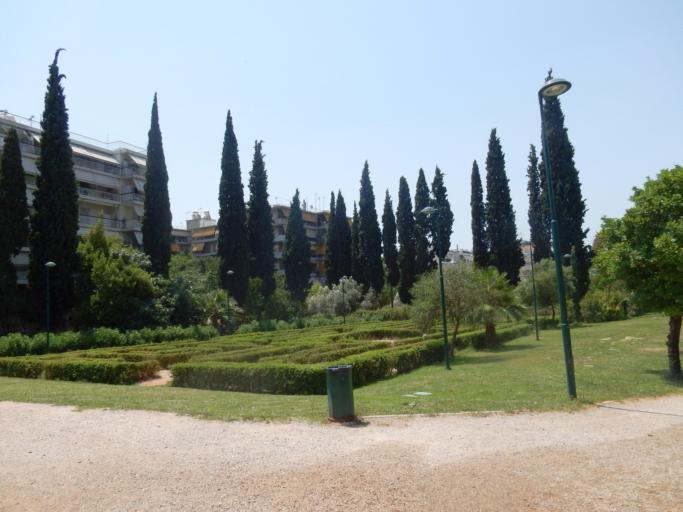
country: GR
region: Attica
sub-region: Nomarchia Athinas
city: Nea Filadelfeia
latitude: 38.0310
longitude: 23.7403
